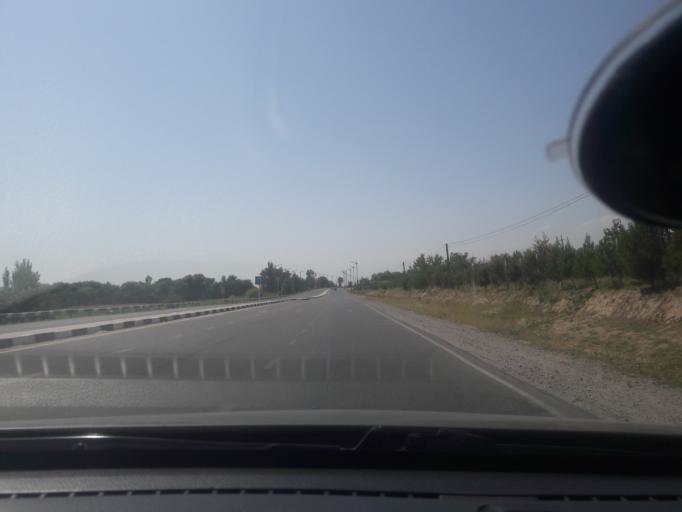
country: TJ
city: Shahrinav
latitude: 38.5641
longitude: 68.4093
